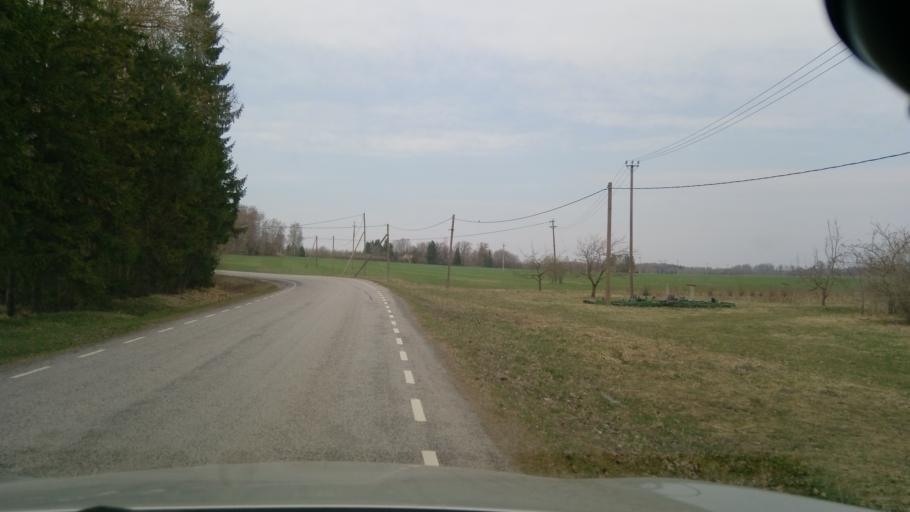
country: EE
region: Jaervamaa
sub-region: Tueri vald
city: Sarevere
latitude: 58.7828
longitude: 25.4786
